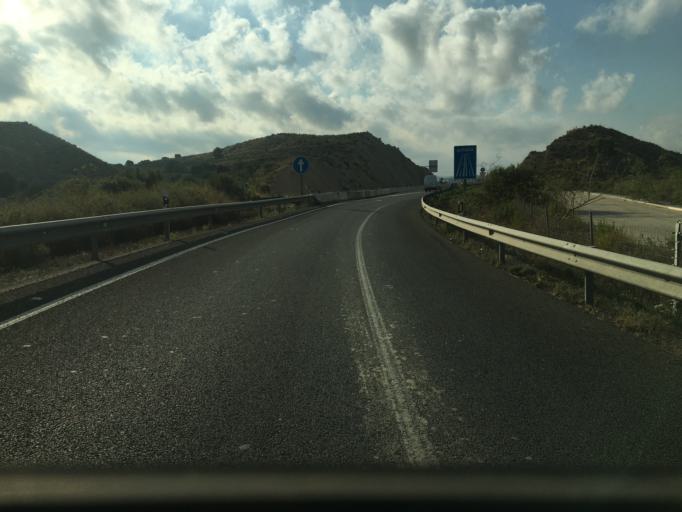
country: ES
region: Murcia
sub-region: Murcia
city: Beniel
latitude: 38.0011
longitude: -1.0120
